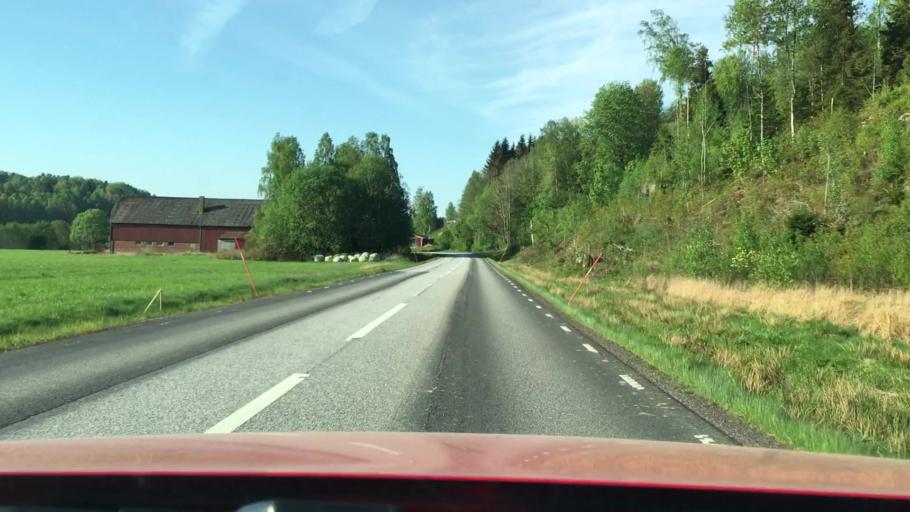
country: SE
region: Vaestra Goetaland
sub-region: Munkedals Kommun
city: Munkedal
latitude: 58.6230
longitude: 11.5592
